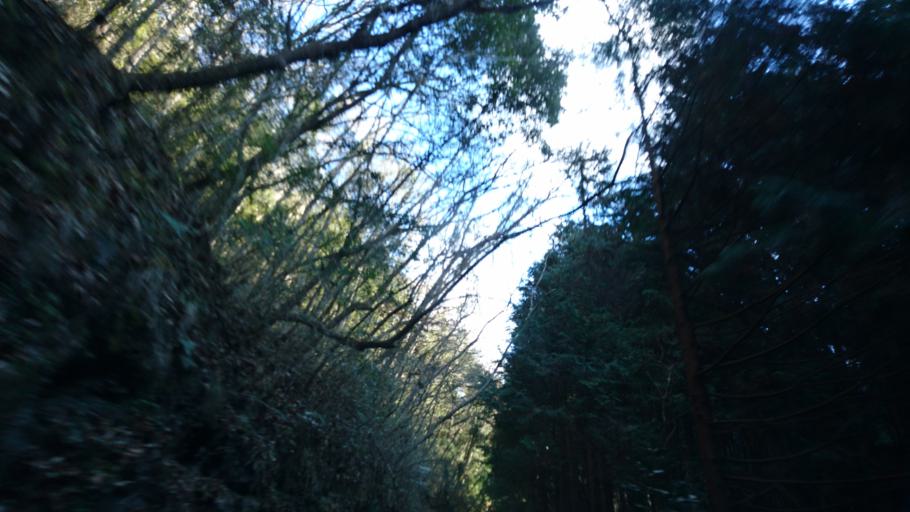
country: JP
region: Okayama
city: Takahashi
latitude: 34.8649
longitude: 133.5683
